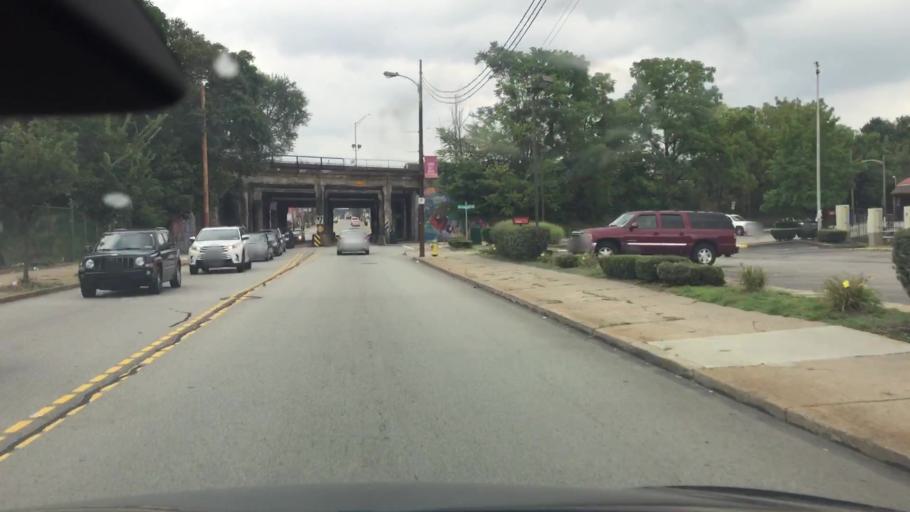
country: US
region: Pennsylvania
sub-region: Allegheny County
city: Wilkinsburg
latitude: 40.4450
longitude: -79.8887
